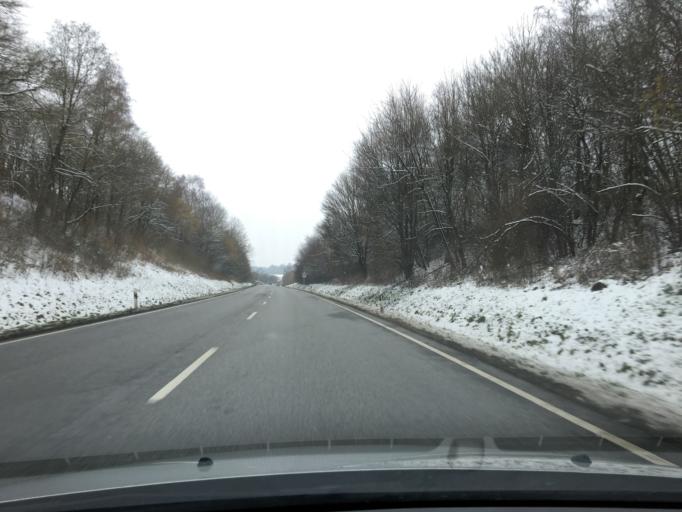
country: DE
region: Bavaria
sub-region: Lower Bavaria
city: Geisenhausen
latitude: 48.4839
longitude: 12.2563
